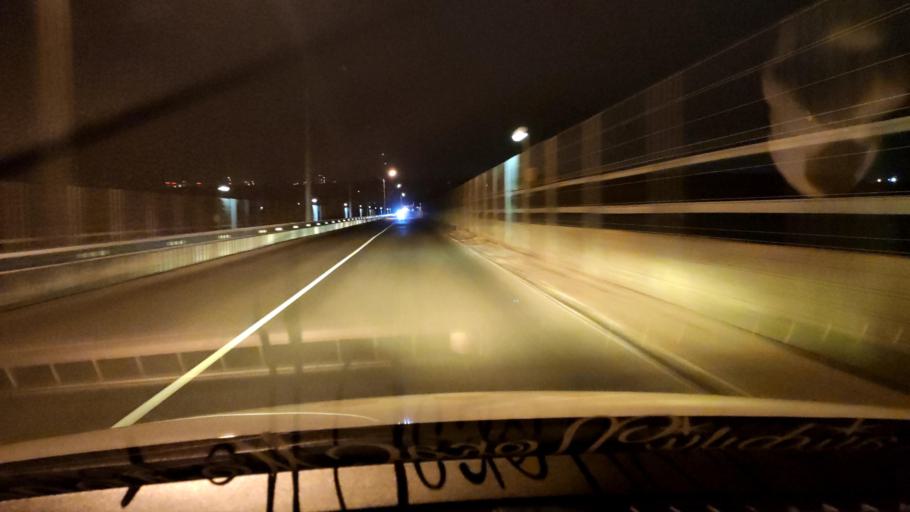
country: RU
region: Voronezj
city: Shilovo
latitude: 51.5451
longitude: 39.1366
